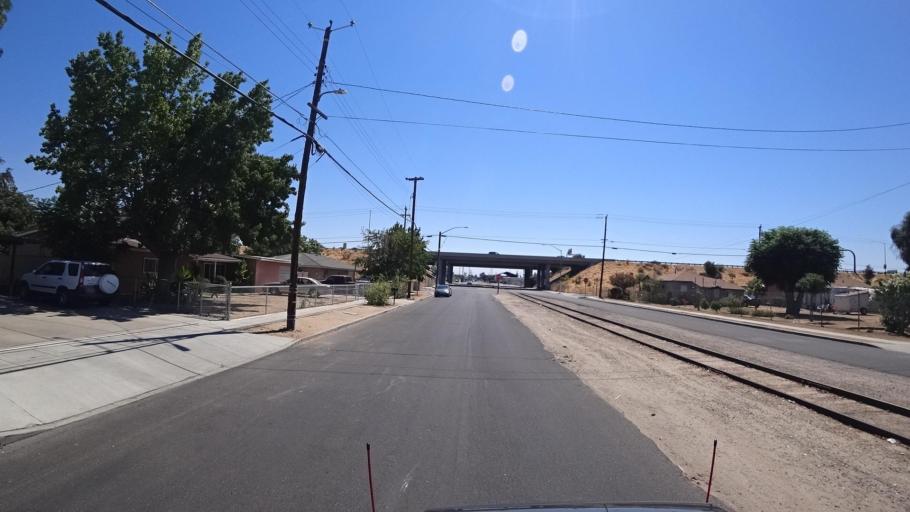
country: US
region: California
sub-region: Fresno County
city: Fresno
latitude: 36.7614
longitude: -119.7507
